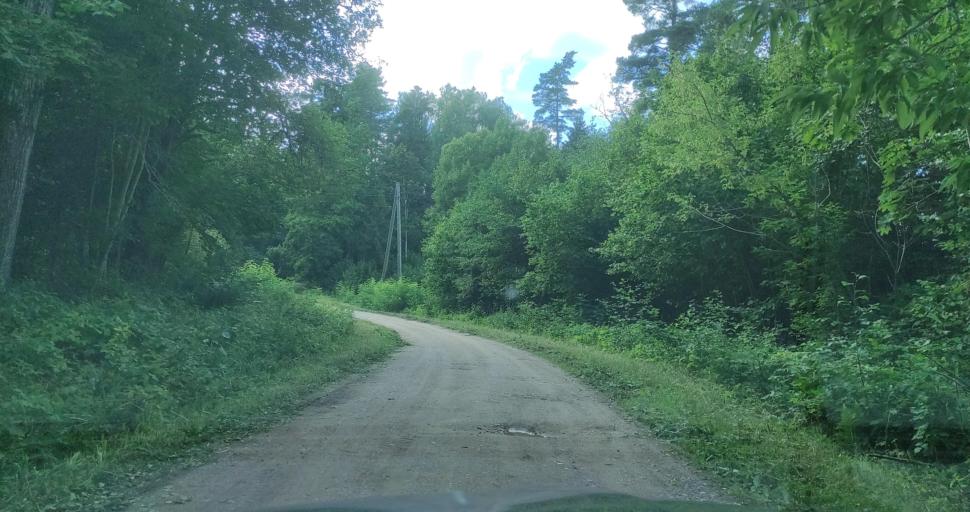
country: LV
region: Kuldigas Rajons
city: Kuldiga
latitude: 56.9907
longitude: 22.0150
